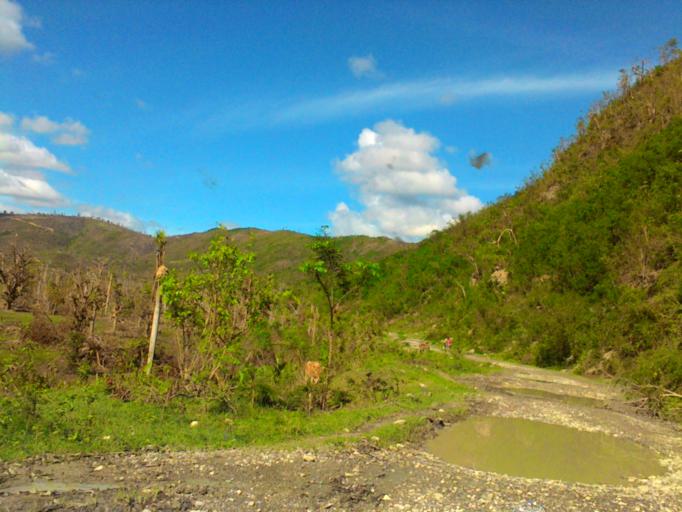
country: HT
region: Grandans
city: Jeremie
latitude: 18.5969
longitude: -74.0957
